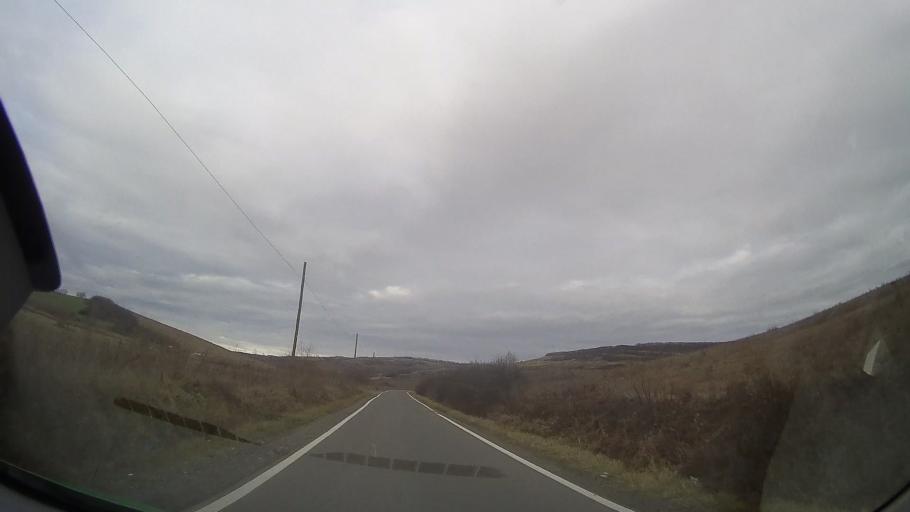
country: RO
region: Mures
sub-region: Comuna Cozma
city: Cozma
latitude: 46.7914
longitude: 24.5433
